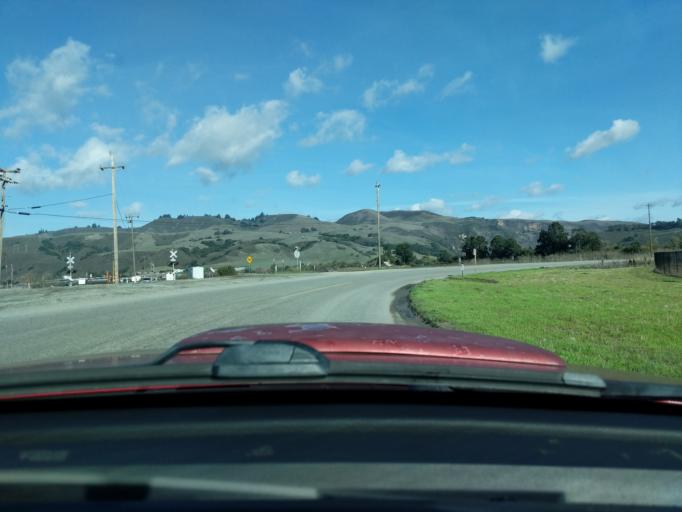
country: US
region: California
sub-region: San Benito County
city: Aromas
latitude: 36.8894
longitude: -121.6512
